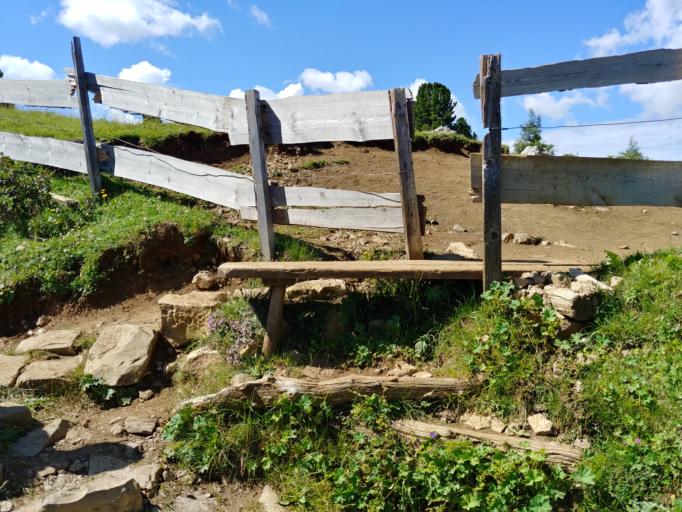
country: IT
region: Trentino-Alto Adige
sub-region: Bolzano
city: Santa Cristina Valgardena
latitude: 46.5195
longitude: 11.6993
